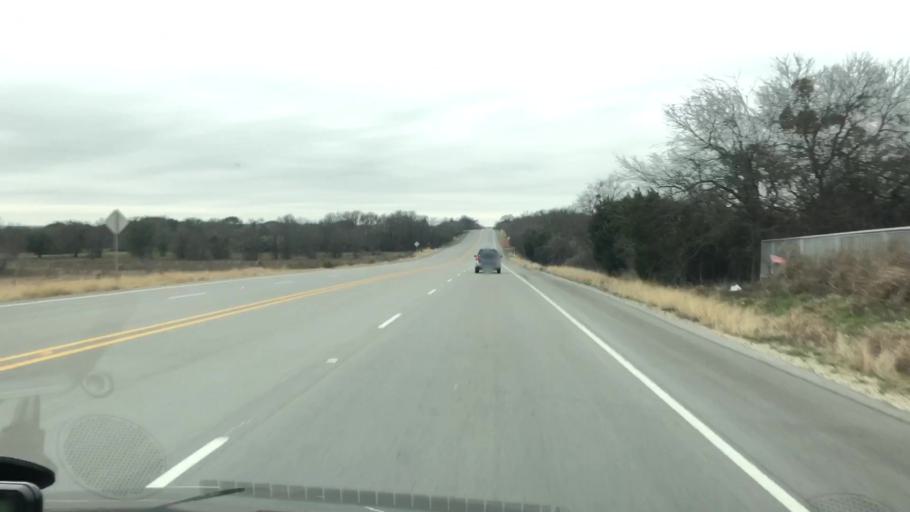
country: US
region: Texas
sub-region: Hamilton County
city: Hico
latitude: 32.0058
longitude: -98.0565
